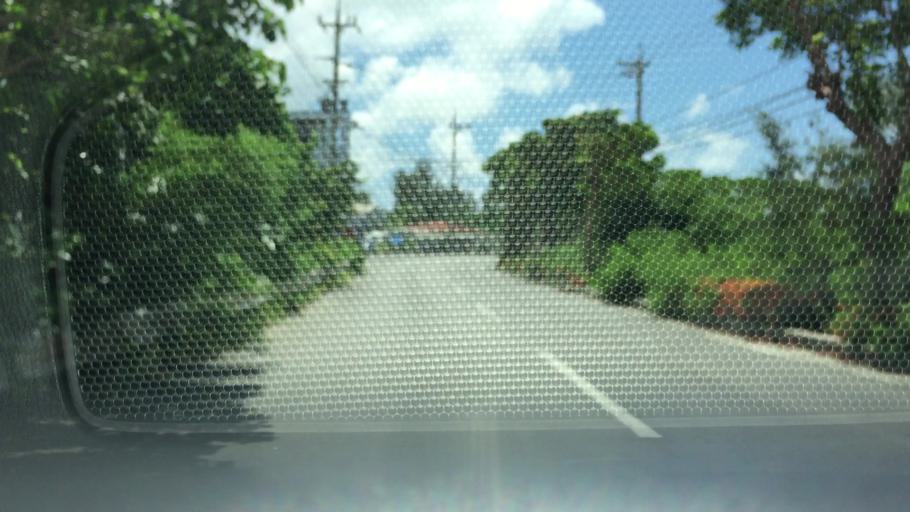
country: JP
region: Okinawa
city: Ishigaki
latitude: 24.3622
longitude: 124.1176
